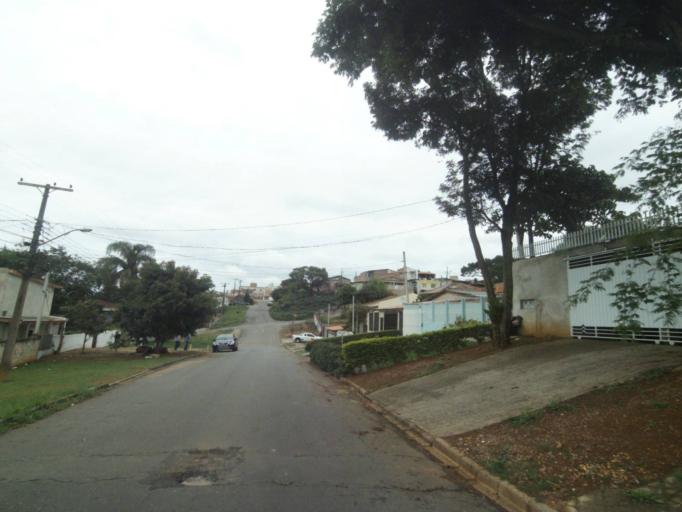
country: BR
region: Parana
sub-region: Curitiba
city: Curitiba
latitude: -25.4555
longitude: -49.3242
